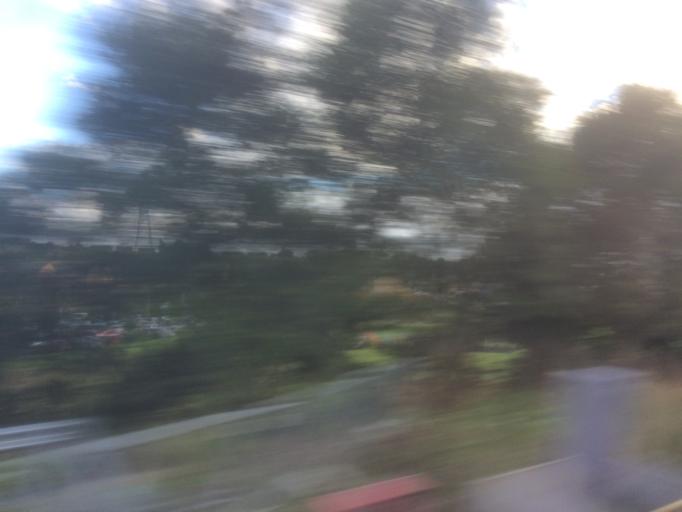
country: GB
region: Scotland
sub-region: North Lanarkshire
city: Kilsyth
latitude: 55.9551
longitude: -4.0373
